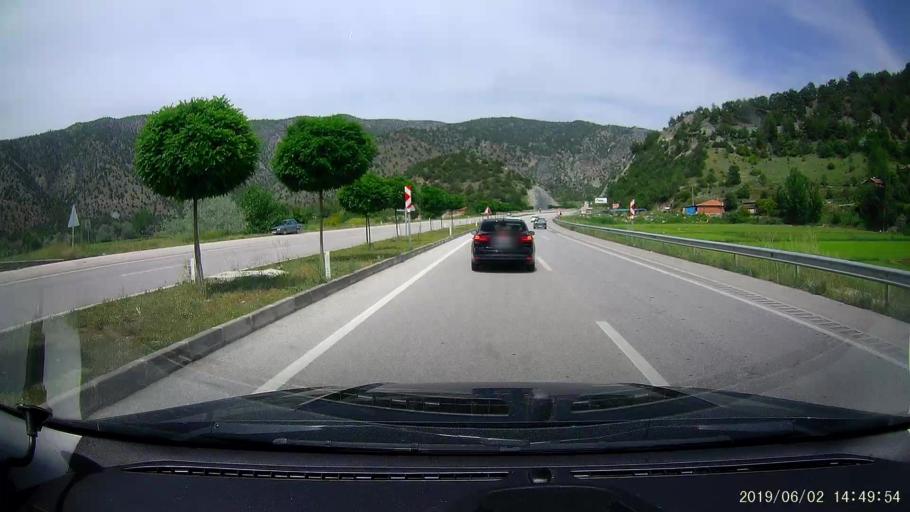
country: TR
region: Corum
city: Hacihamza
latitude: 41.0706
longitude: 34.5085
